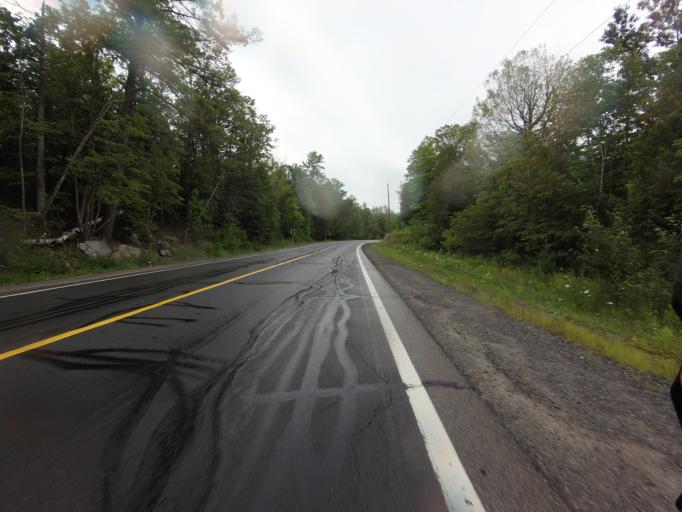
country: CA
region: Ontario
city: Perth
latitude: 44.9945
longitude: -76.3880
